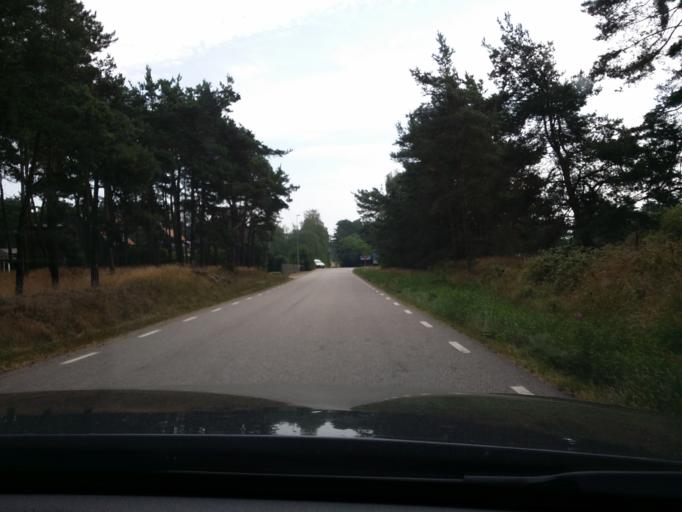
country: SE
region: Blekinge
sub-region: Solvesborgs Kommun
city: Soelvesborg
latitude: 56.0249
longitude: 14.7172
